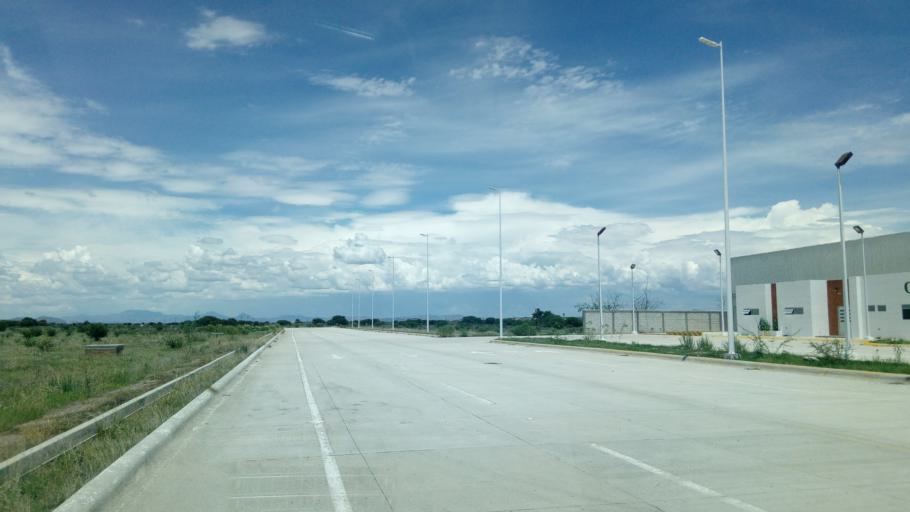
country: MX
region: Durango
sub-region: Durango
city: Jose Refugio Salcido
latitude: 24.1600
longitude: -104.5120
